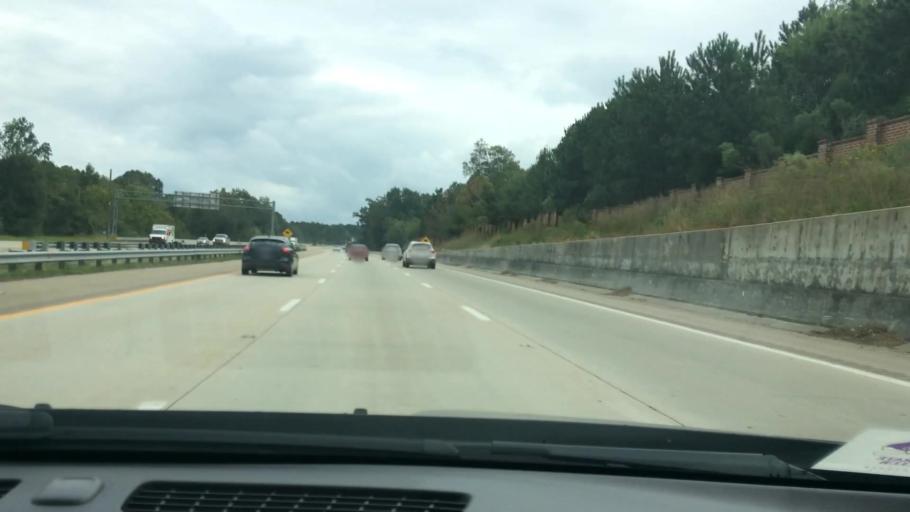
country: US
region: North Carolina
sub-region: Wake County
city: Knightdale
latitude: 35.7729
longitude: -78.5421
